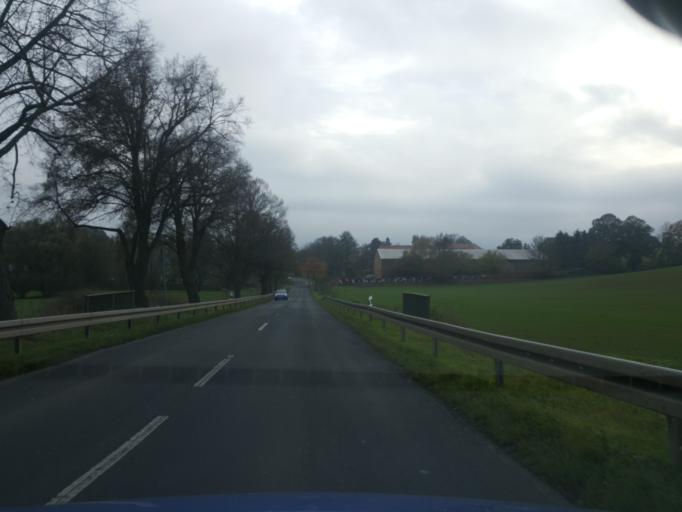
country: DE
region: Saxony-Anhalt
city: Volkstedt
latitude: 51.5539
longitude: 11.5458
